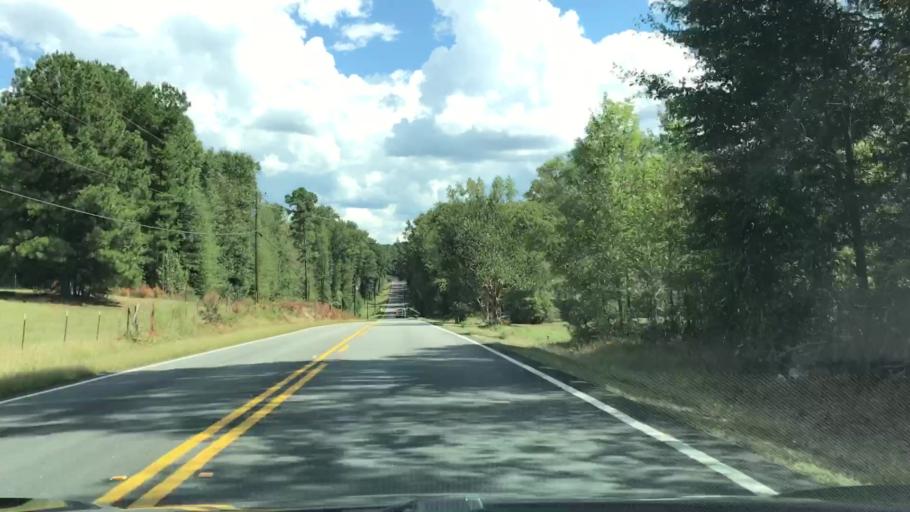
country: US
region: Georgia
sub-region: Greene County
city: Greensboro
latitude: 33.5591
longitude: -83.1189
